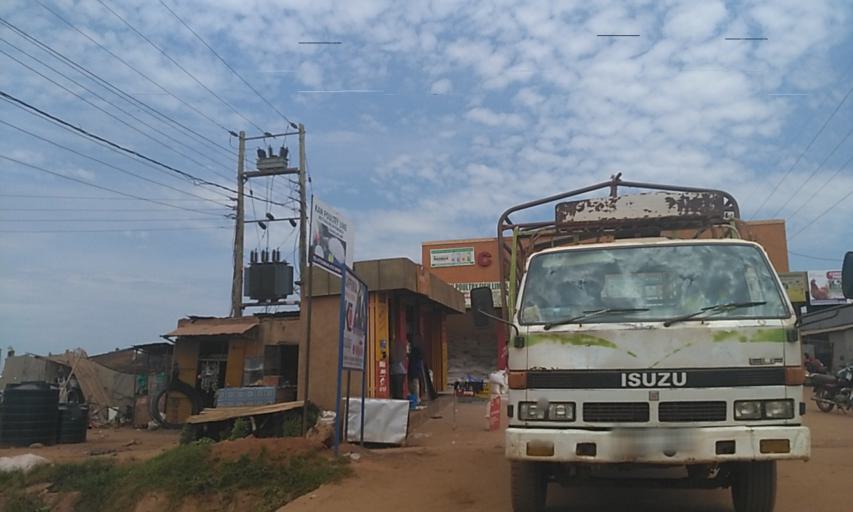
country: UG
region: Central Region
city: Kampala Central Division
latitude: 0.2977
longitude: 32.5280
